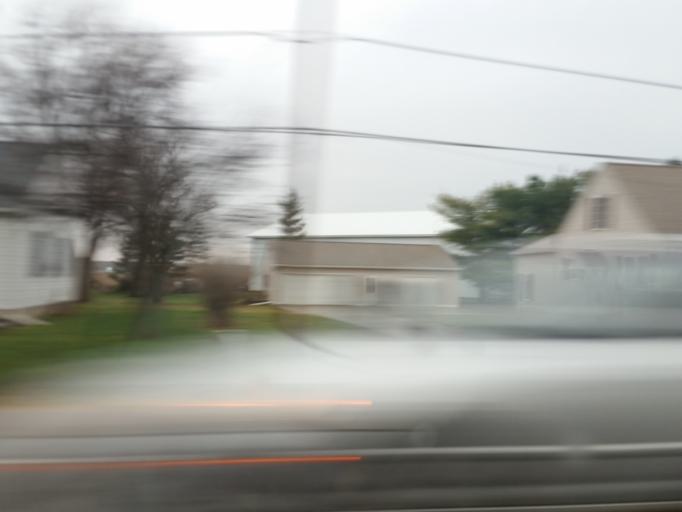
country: US
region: Iowa
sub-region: Black Hawk County
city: Elk Run Heights
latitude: 42.4180
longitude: -92.2733
